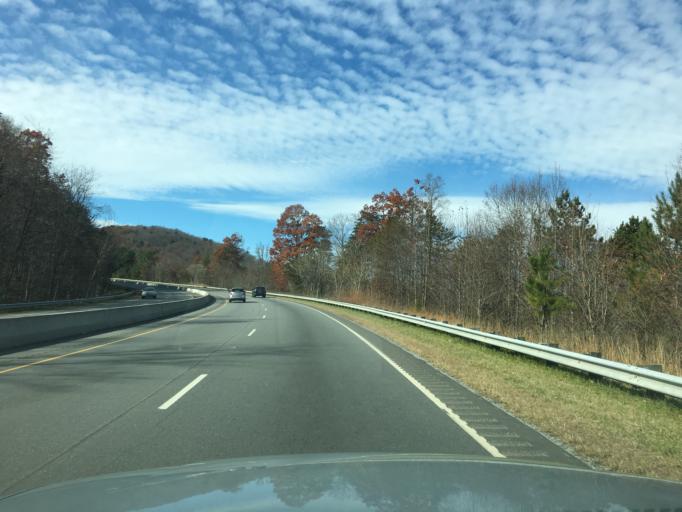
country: US
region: North Carolina
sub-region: McDowell County
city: Marion
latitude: 35.6689
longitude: -81.9907
